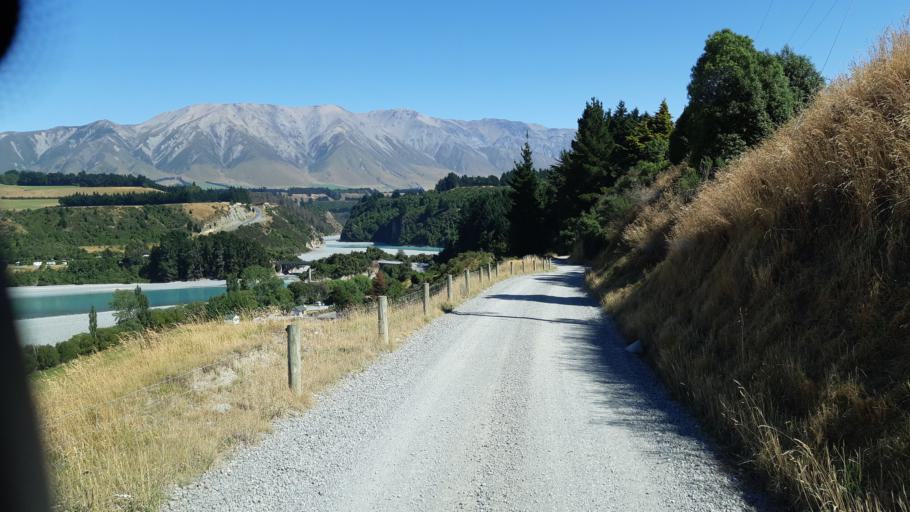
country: NZ
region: Canterbury
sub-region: Ashburton District
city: Methven
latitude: -43.5200
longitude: 171.6640
